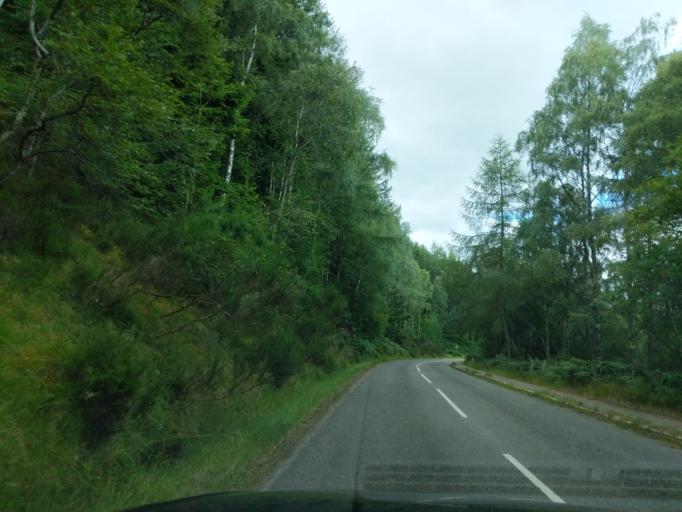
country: GB
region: Scotland
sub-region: Aberdeenshire
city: Ballater
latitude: 57.0566
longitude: -3.0029
